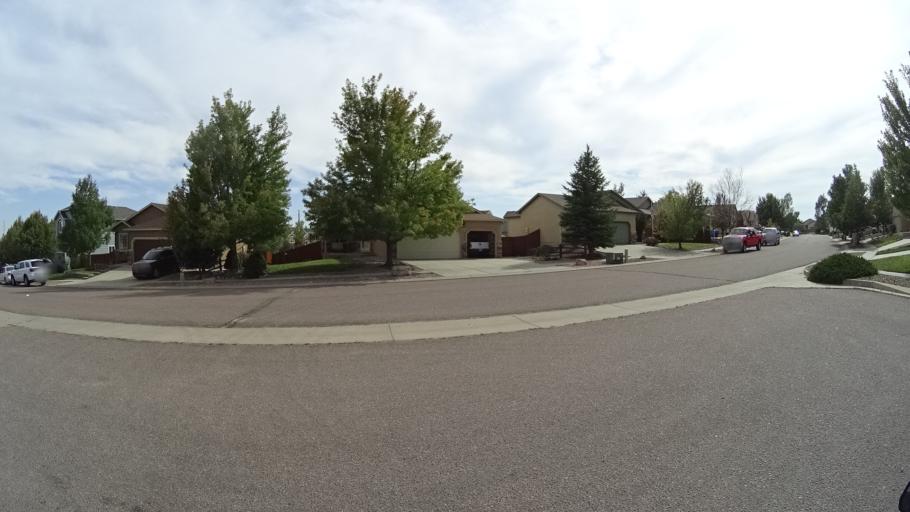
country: US
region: Colorado
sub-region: El Paso County
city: Cimarron Hills
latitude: 38.9036
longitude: -104.6883
